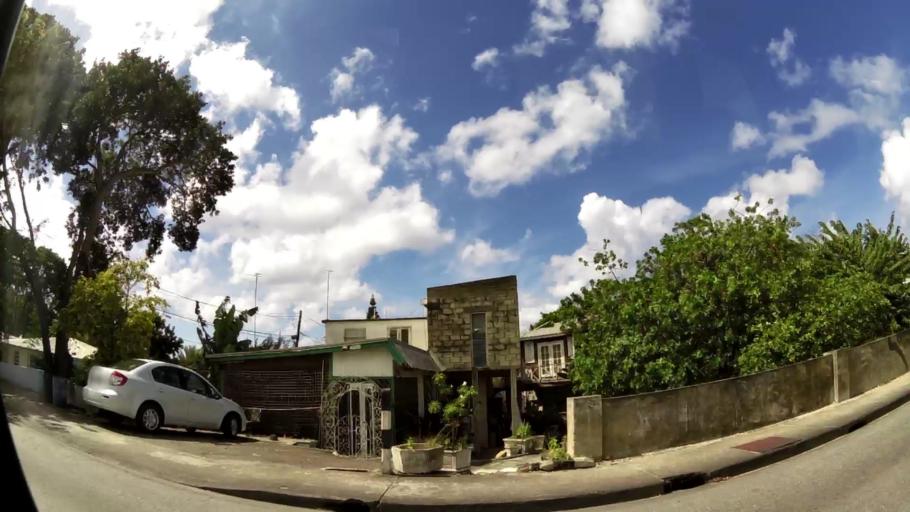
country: BB
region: Saint James
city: Holetown
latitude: 13.1440
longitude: -59.6379
